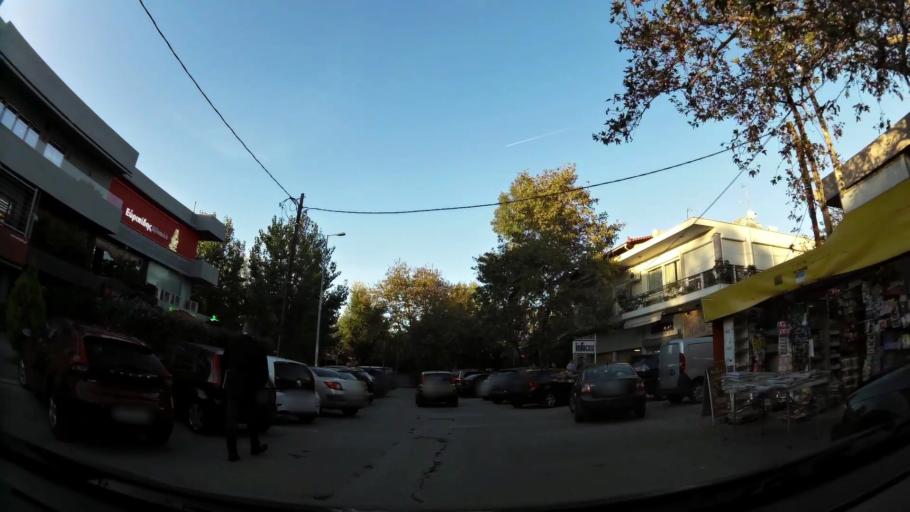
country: GR
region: Attica
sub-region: Nomarchia Athinas
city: Kifisia
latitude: 38.0838
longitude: 23.8167
